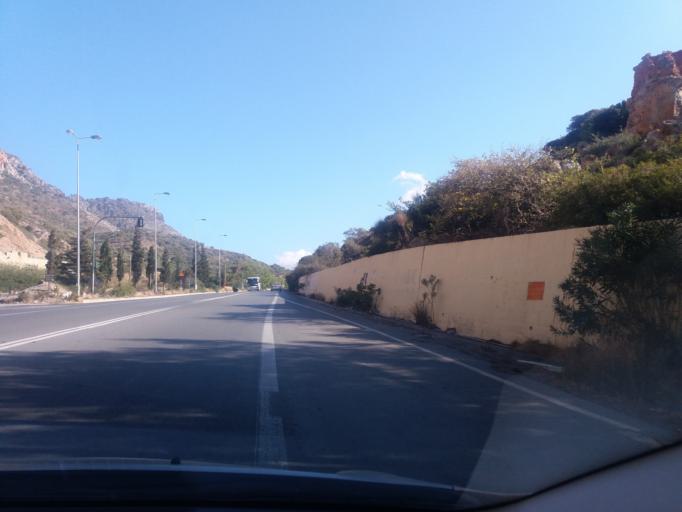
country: GR
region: Crete
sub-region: Nomos Lasithiou
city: Sision
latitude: 35.2845
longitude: 25.5435
